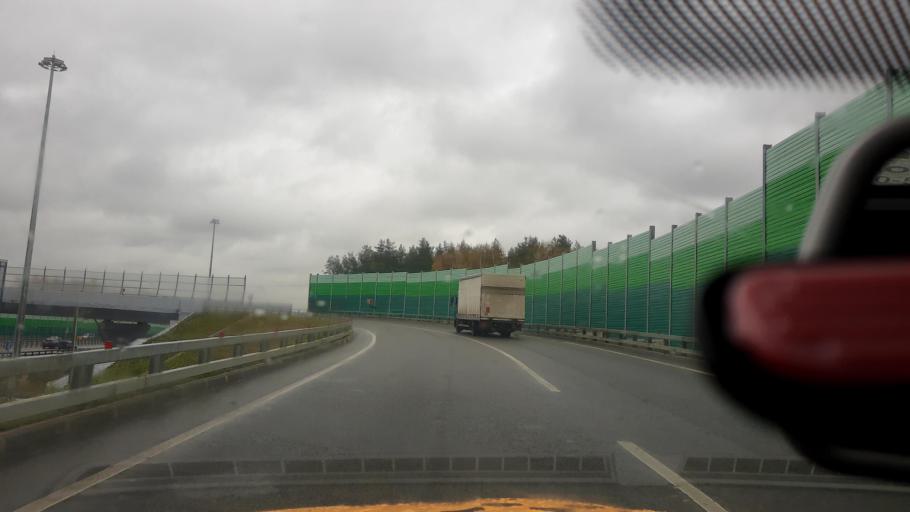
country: RU
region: Moskovskaya
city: Odintsovo
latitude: 55.6523
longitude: 37.2748
